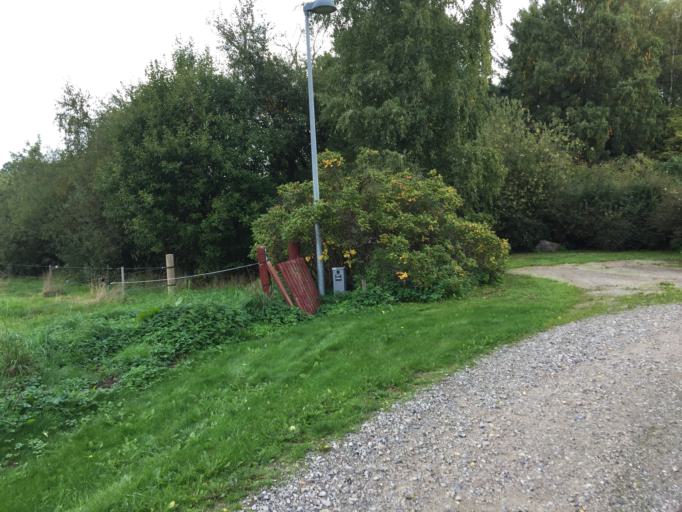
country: DK
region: Capital Region
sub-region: Fureso Kommune
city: Farum
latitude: 55.8269
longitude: 12.3598
